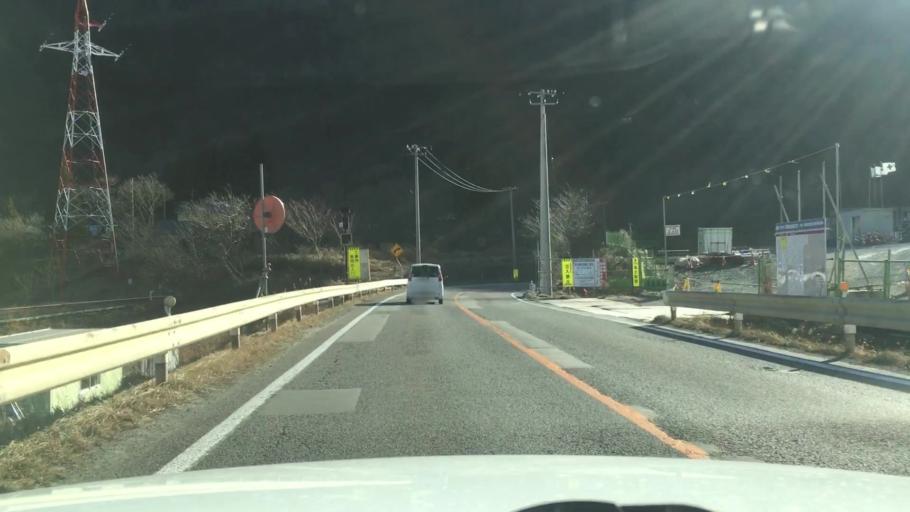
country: JP
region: Iwate
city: Miyako
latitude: 39.5991
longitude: 141.7609
